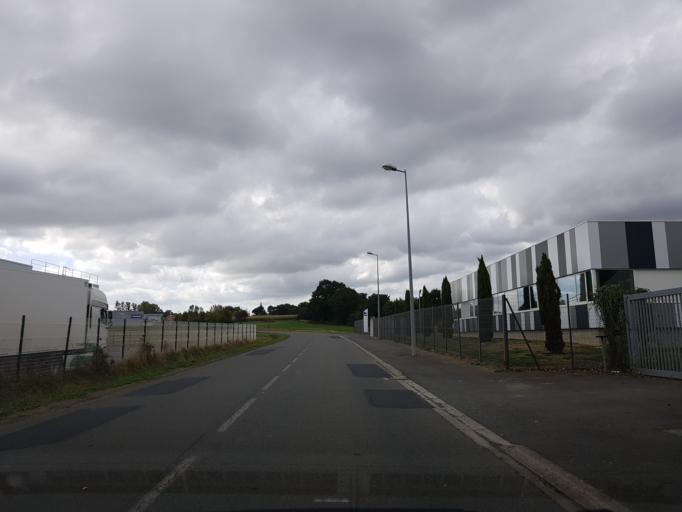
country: FR
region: Brittany
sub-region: Departement des Cotes-d'Armor
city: Pommeret
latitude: 48.4476
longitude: -2.6453
